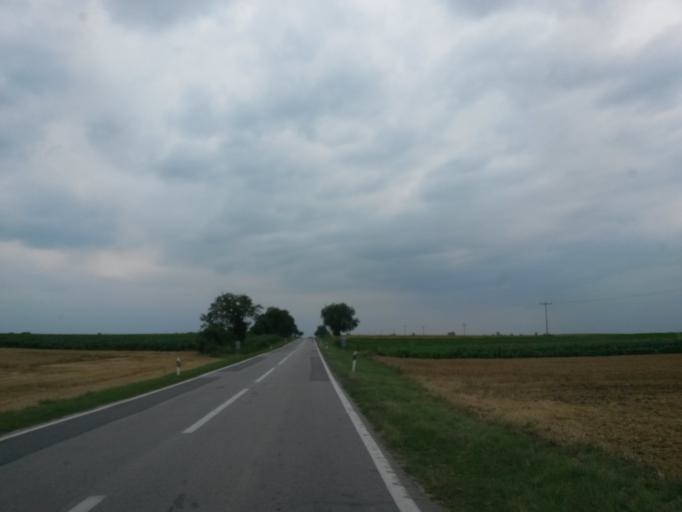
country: HR
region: Vukovarsko-Srijemska
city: Lovas
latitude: 45.2570
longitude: 19.1833
